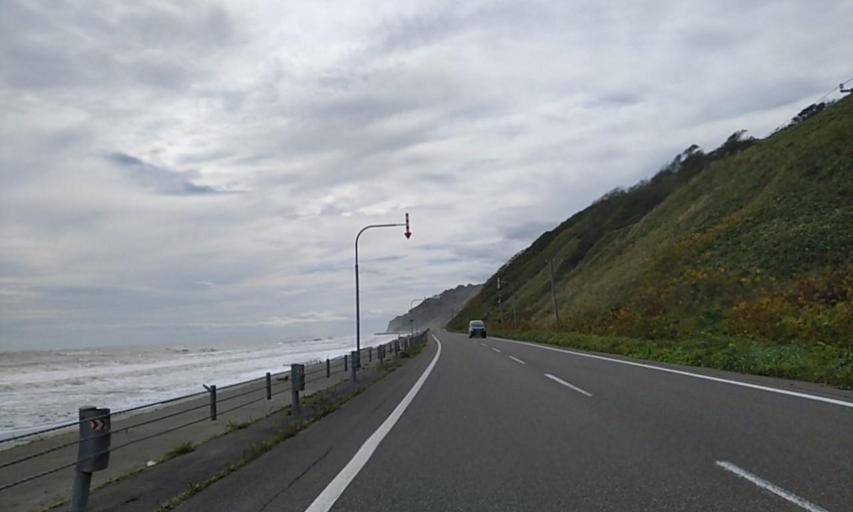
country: JP
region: Hokkaido
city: Obihiro
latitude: 42.7797
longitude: 143.7824
